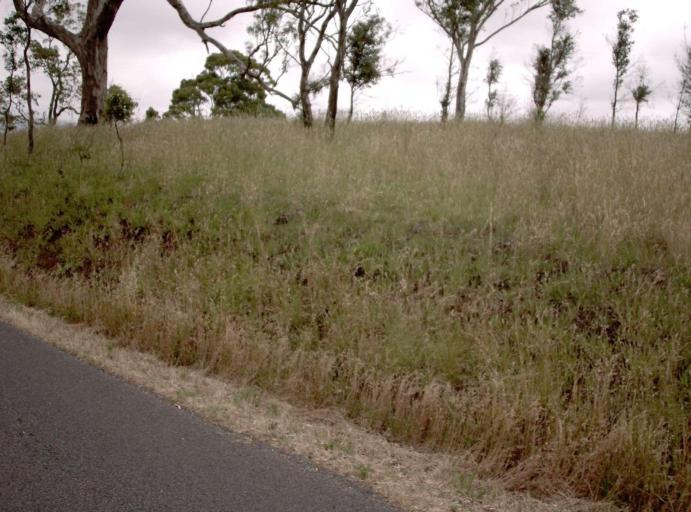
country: AU
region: Victoria
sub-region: Wellington
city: Heyfield
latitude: -37.8711
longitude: 146.7076
